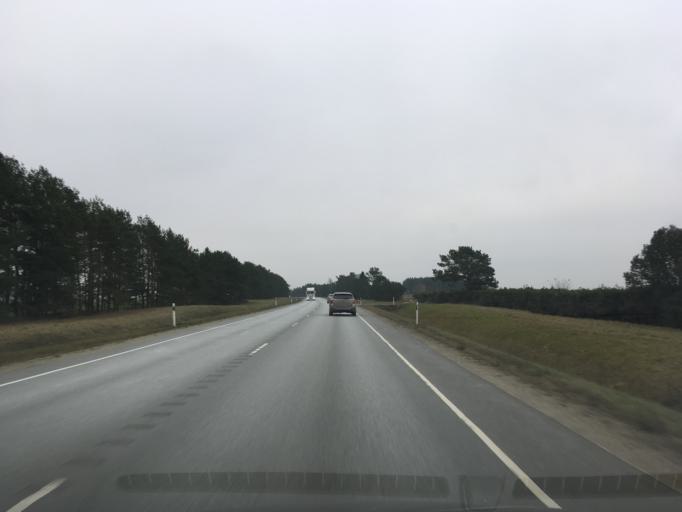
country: EE
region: Ida-Virumaa
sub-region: Puessi linn
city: Pussi
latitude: 59.4090
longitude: 27.0514
